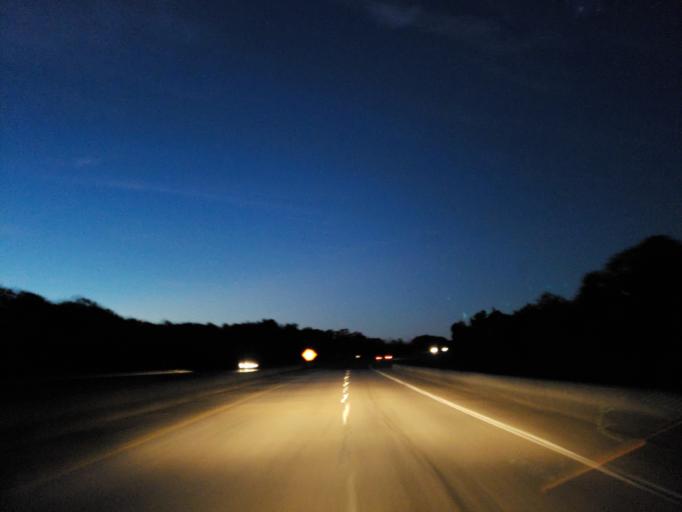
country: US
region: Mississippi
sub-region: Clarke County
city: Quitman
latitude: 32.1129
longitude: -88.7157
